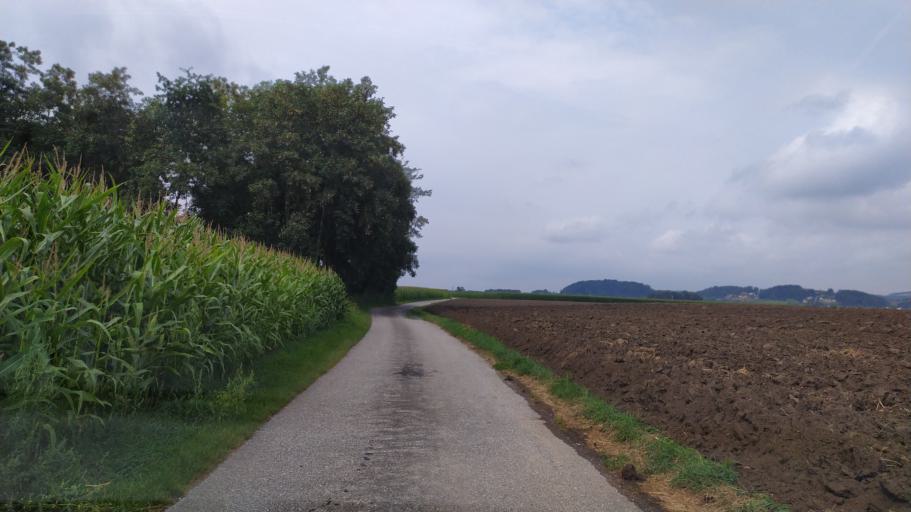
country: AT
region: Upper Austria
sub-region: Politischer Bezirk Perg
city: Bad Kreuzen
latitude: 48.1995
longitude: 14.7784
